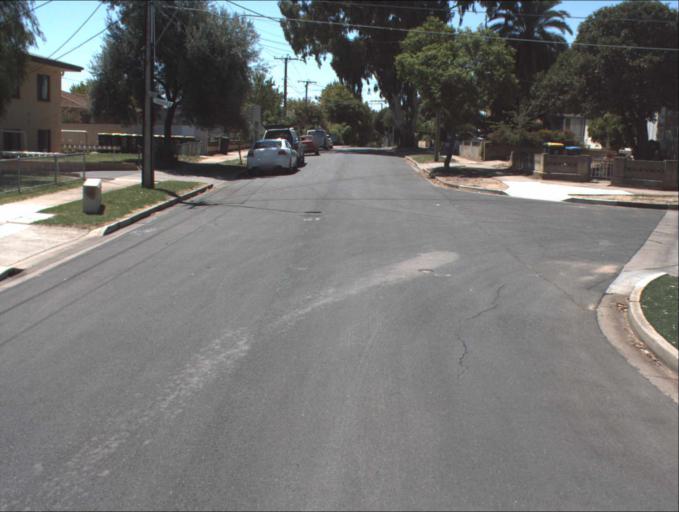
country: AU
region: South Australia
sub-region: Port Adelaide Enfield
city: Blair Athol
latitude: -34.8687
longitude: 138.6069
